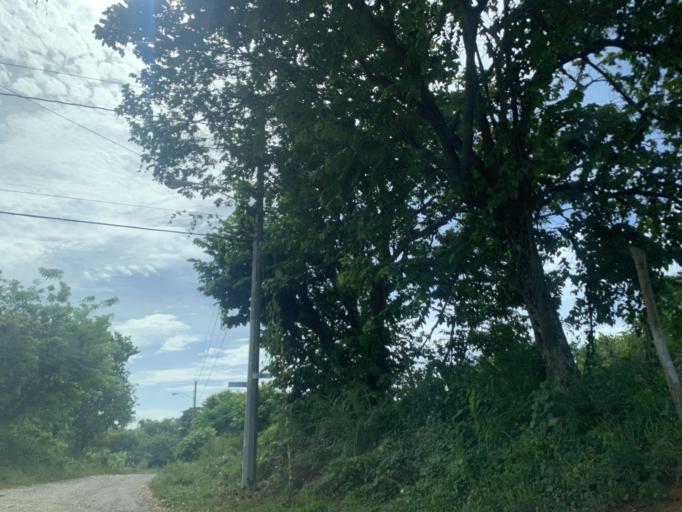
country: DO
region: Puerto Plata
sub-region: Puerto Plata
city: Puerto Plata
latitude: 19.8147
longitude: -70.7195
